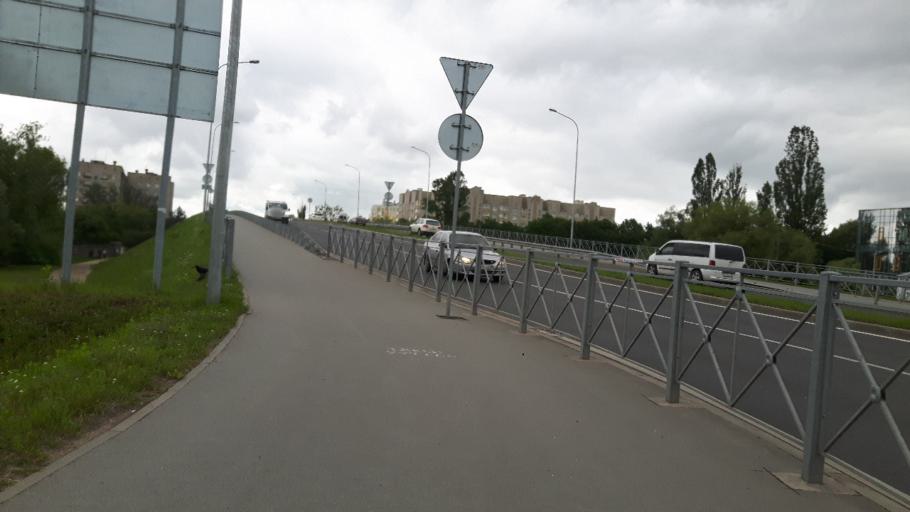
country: RU
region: Kaliningrad
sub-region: Gorod Kaliningrad
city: Kaliningrad
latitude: 54.7365
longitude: 20.4935
